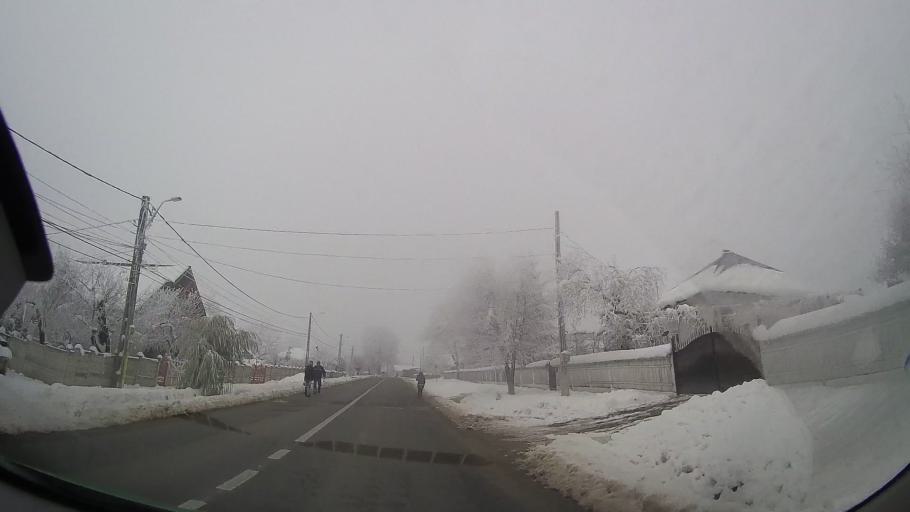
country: RO
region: Iasi
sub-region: Comuna Stolniceni-Prajescu
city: Stolniceni-Prajescu
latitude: 47.1699
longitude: 26.7666
